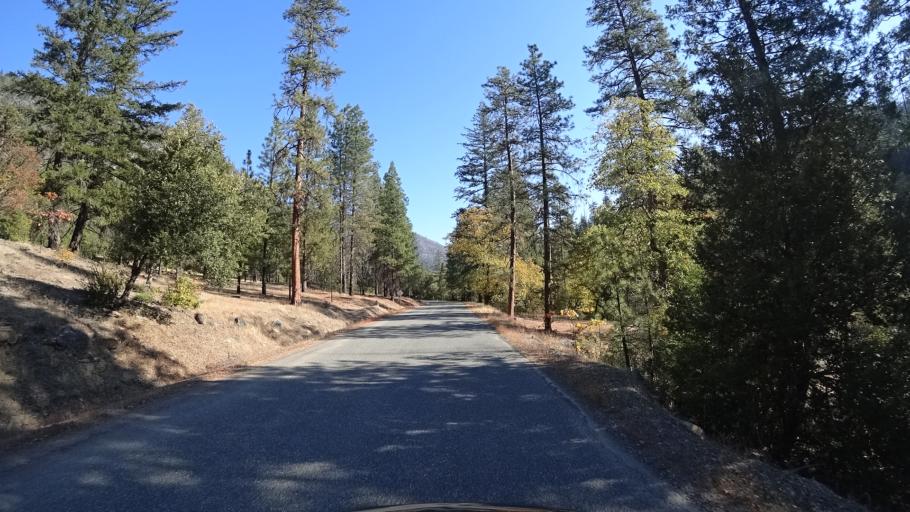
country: US
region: California
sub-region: Siskiyou County
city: Happy Camp
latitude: 41.6836
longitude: -123.0920
